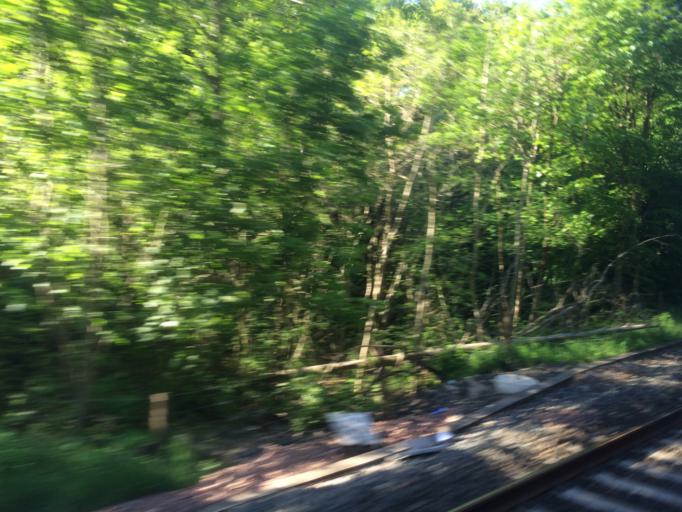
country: GB
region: Scotland
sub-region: North Lanarkshire
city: Cumbernauld
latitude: 55.9475
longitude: -3.9669
